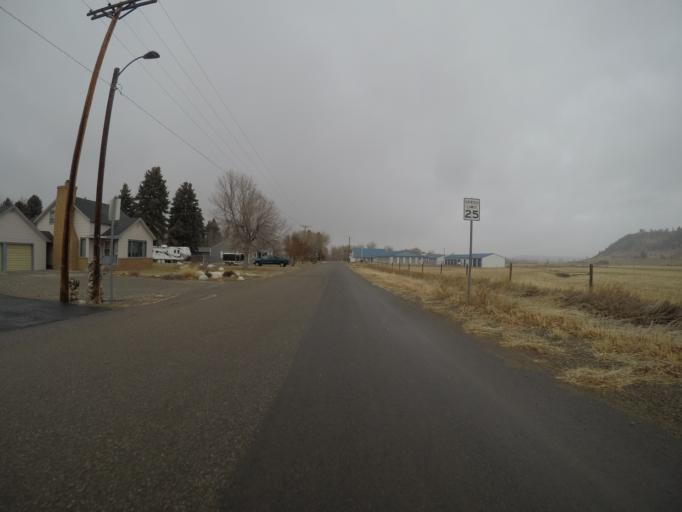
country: US
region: Montana
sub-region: Stillwater County
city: Absarokee
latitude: 45.5239
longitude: -109.4386
